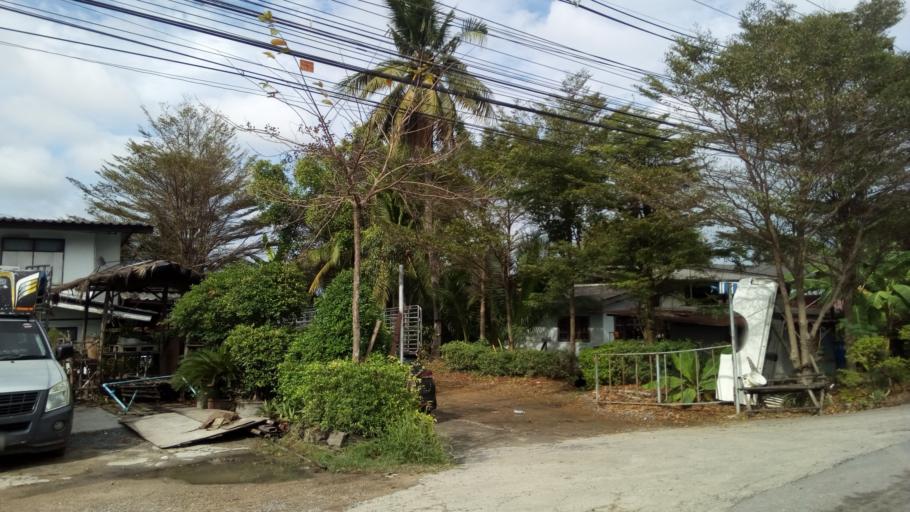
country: TH
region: Nakhon Nayok
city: Ongkharak
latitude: 14.0887
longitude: 100.9271
